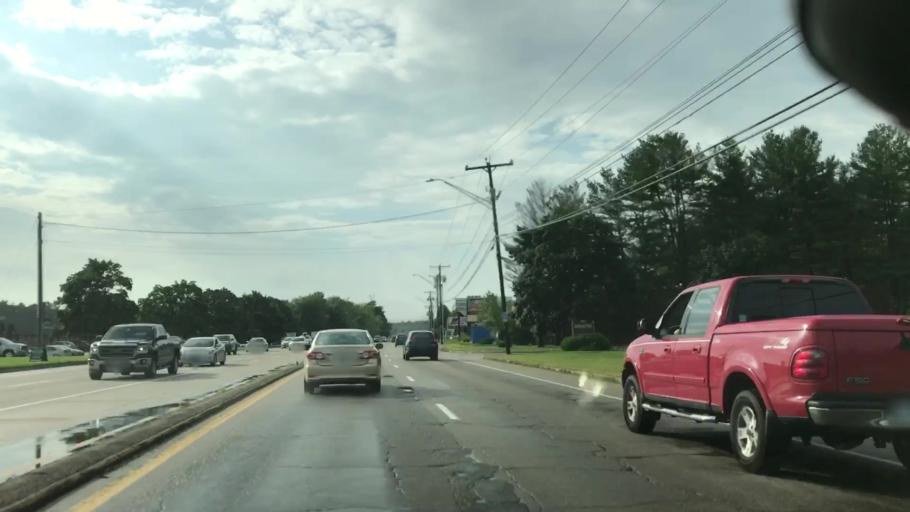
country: US
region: New Hampshire
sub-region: Hillsborough County
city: Nashua
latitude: 42.7949
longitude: -71.5266
